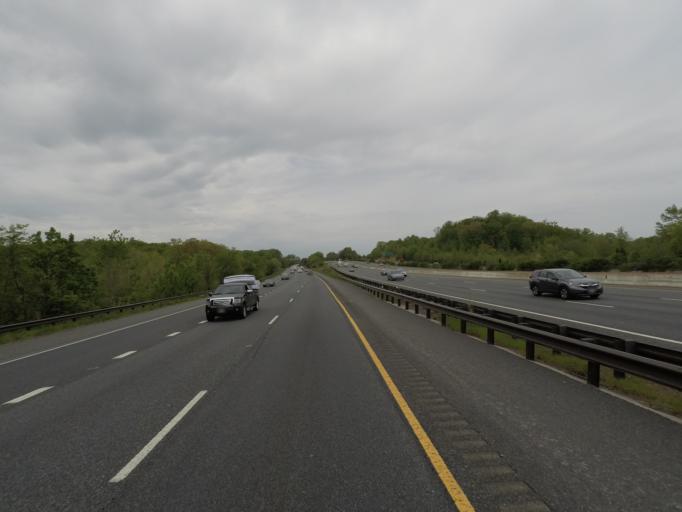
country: US
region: Maryland
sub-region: Anne Arundel County
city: Edgewater
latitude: 38.9834
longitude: -76.5671
